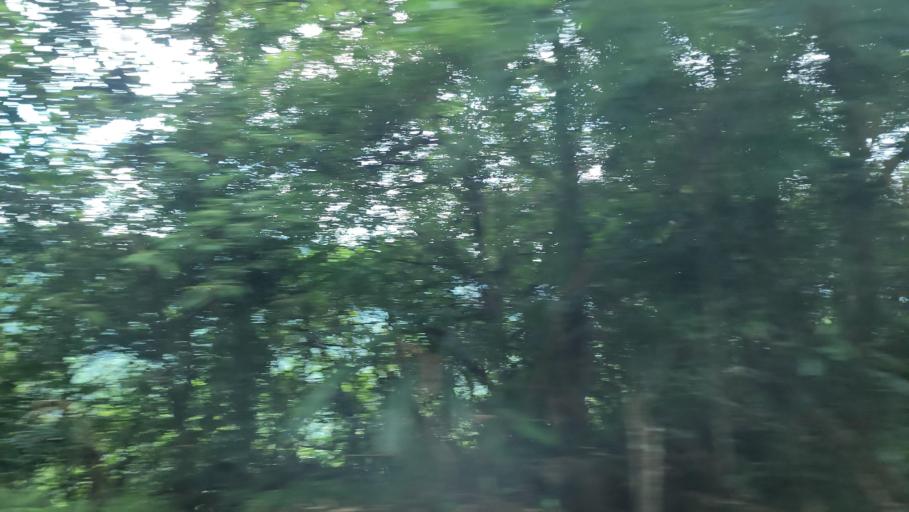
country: TW
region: Taipei
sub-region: Taipei
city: Banqiao
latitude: 24.8903
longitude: 121.4268
